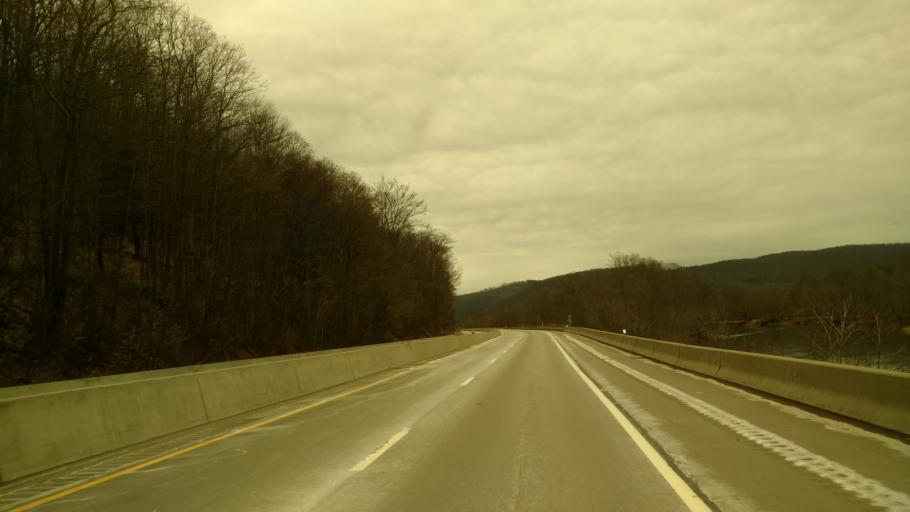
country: US
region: New York
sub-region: Cattaraugus County
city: Salamanca
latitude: 42.1328
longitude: -78.6659
